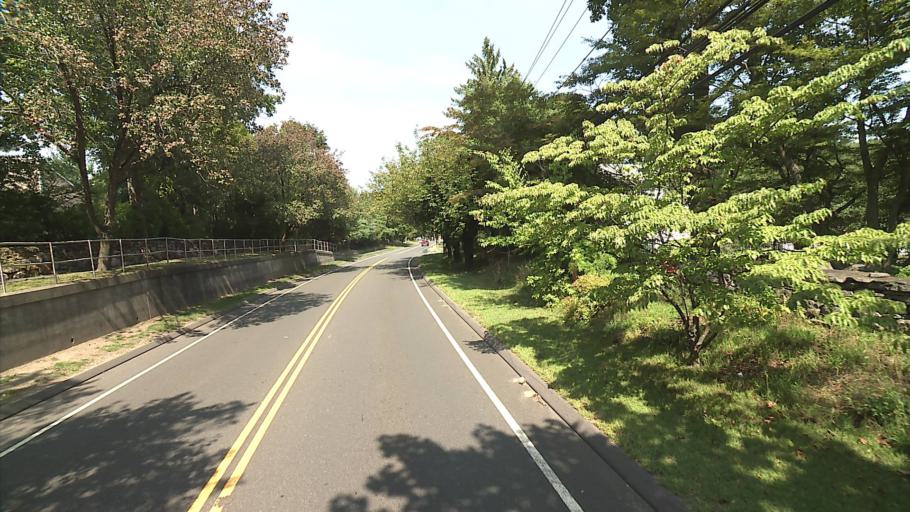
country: US
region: Connecticut
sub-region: Fairfield County
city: Fairfield
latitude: 41.1627
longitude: -73.2549
